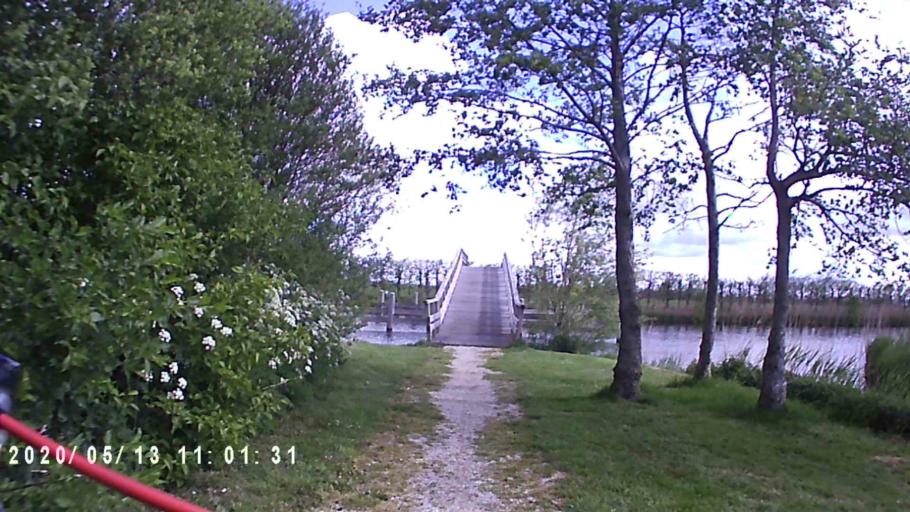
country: NL
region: Groningen
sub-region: Gemeente Zuidhorn
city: Grijpskerk
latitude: 53.2836
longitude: 6.3279
